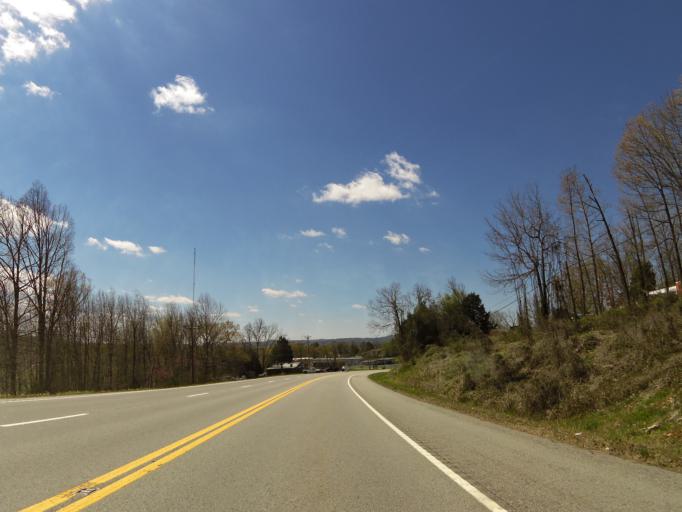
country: US
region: Tennessee
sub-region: White County
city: Sparta
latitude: 35.9240
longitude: -85.4435
